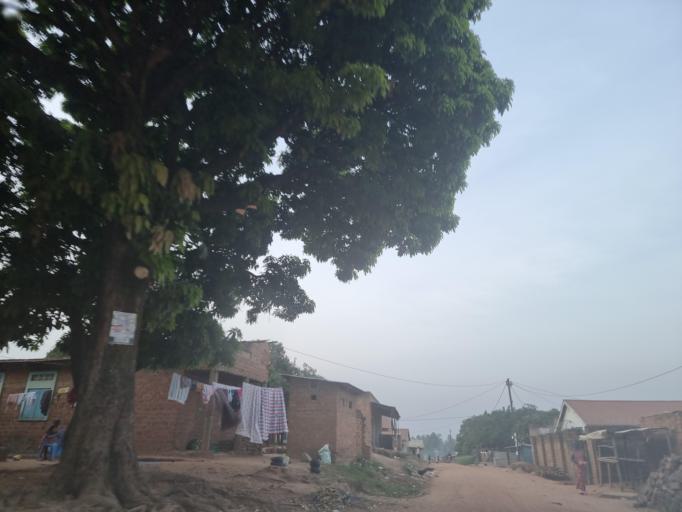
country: UG
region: Northern Region
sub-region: Arua District
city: Arua
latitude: 3.0323
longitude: 30.9111
